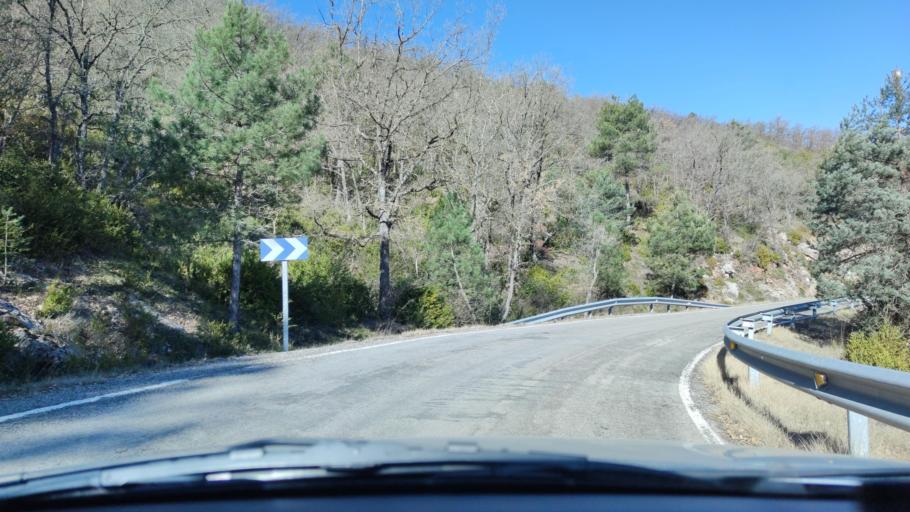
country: ES
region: Catalonia
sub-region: Provincia de Lleida
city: Llimiana
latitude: 42.0414
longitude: 1.0461
